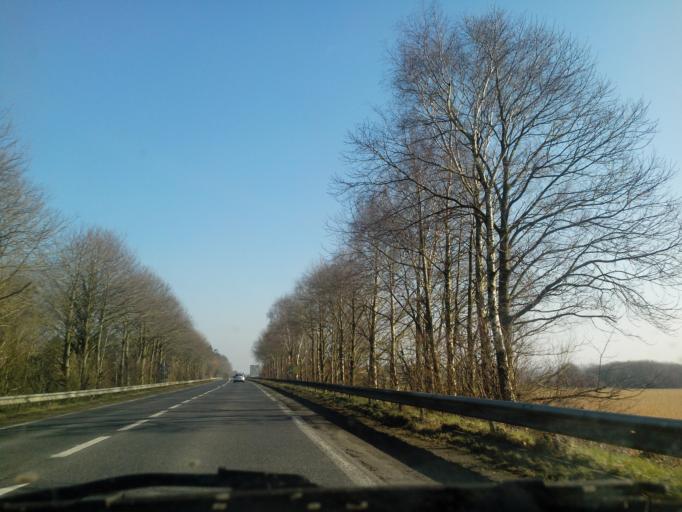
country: FR
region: Brittany
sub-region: Departement des Cotes-d'Armor
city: Merdrignac
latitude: 48.1914
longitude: -2.4388
